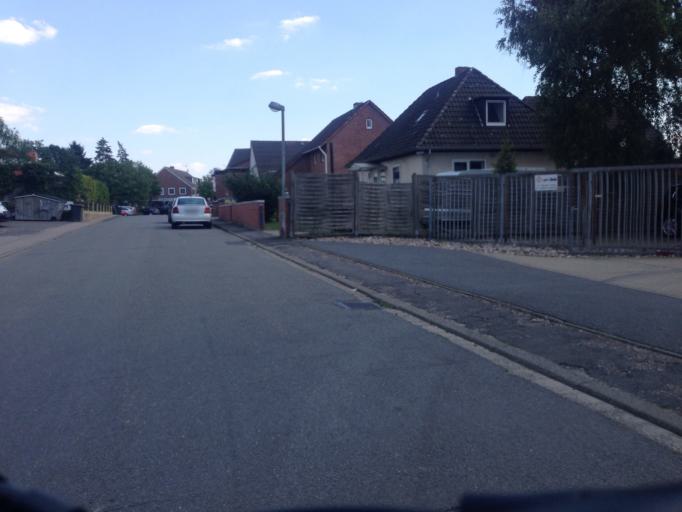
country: DE
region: Lower Saxony
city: Adendorf
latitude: 53.2798
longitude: 10.4353
